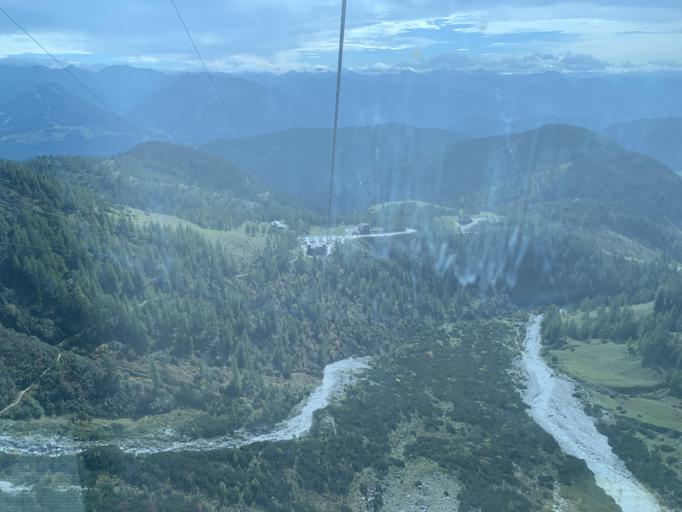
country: AT
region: Styria
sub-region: Politischer Bezirk Liezen
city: Schladming
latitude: 47.4577
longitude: 13.6212
